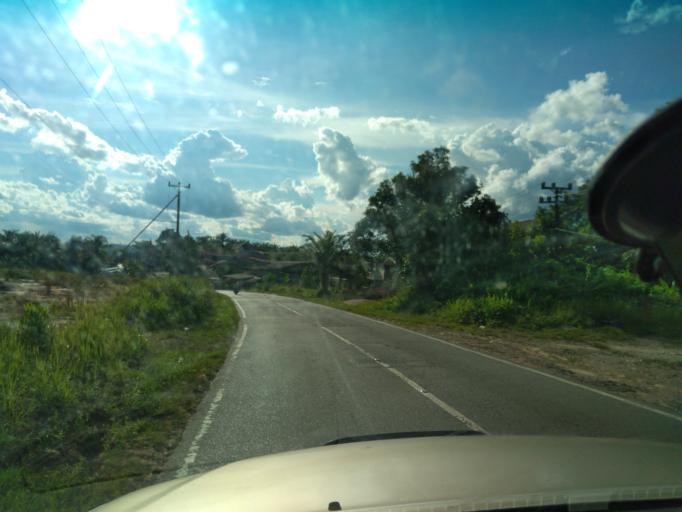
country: ID
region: West Kalimantan
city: Tayan
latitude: 0.3762
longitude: 109.9295
